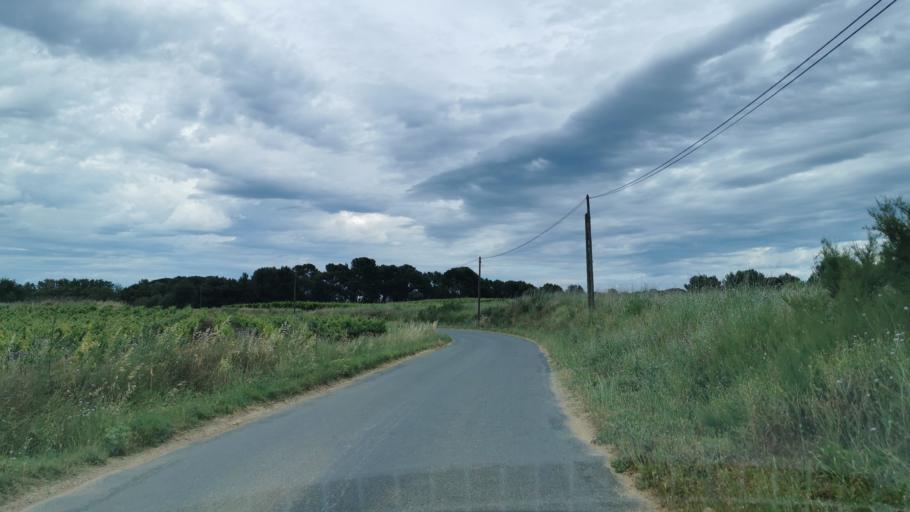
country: FR
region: Languedoc-Roussillon
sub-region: Departement de l'Aude
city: Moussan
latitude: 43.2407
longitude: 2.9643
